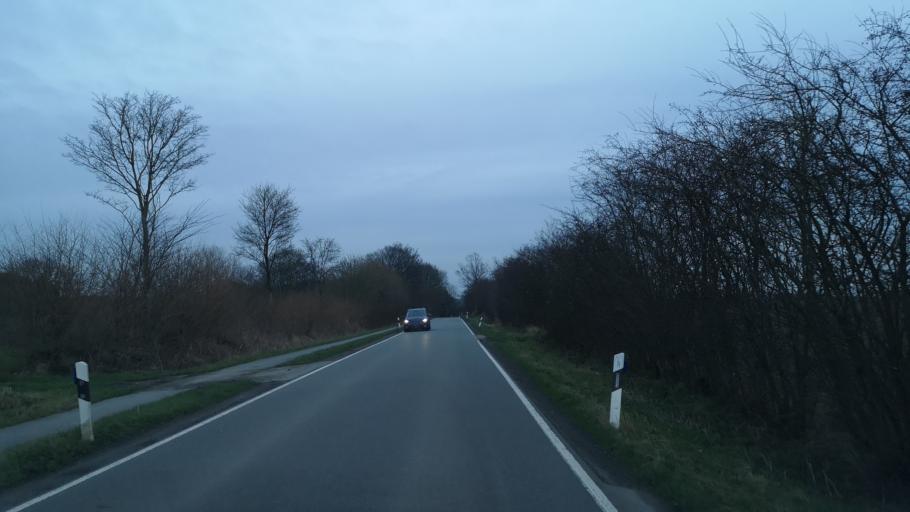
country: DE
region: Schleswig-Holstein
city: Satrup
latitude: 54.6990
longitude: 9.6262
